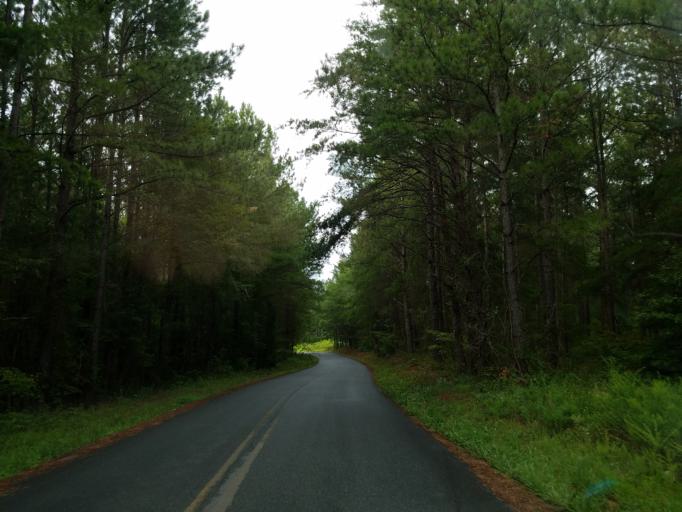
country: US
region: Georgia
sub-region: Bartow County
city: Rydal
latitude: 34.3824
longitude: -84.6684
